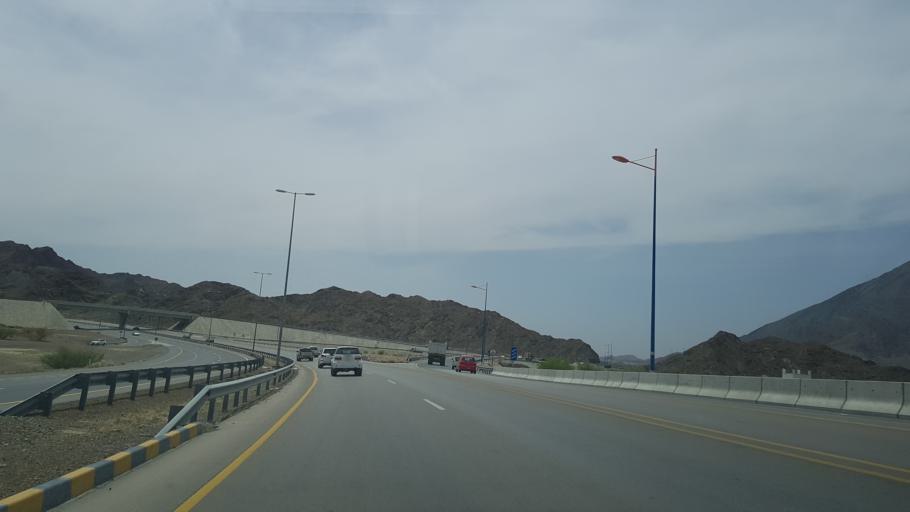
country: OM
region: Muhafazat ad Dakhiliyah
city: Izki
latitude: 22.9749
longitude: 57.7805
